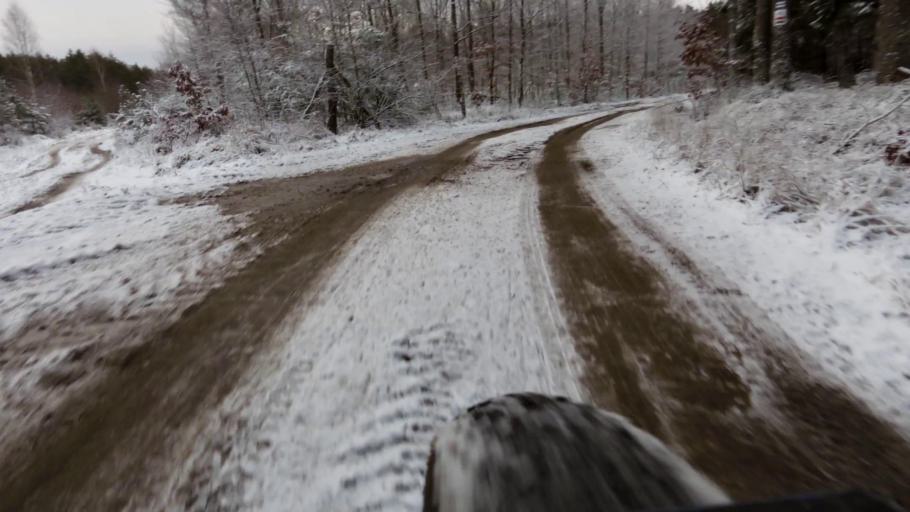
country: PL
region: West Pomeranian Voivodeship
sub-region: Powiat walecki
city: Miroslawiec
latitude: 53.3772
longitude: 16.1457
